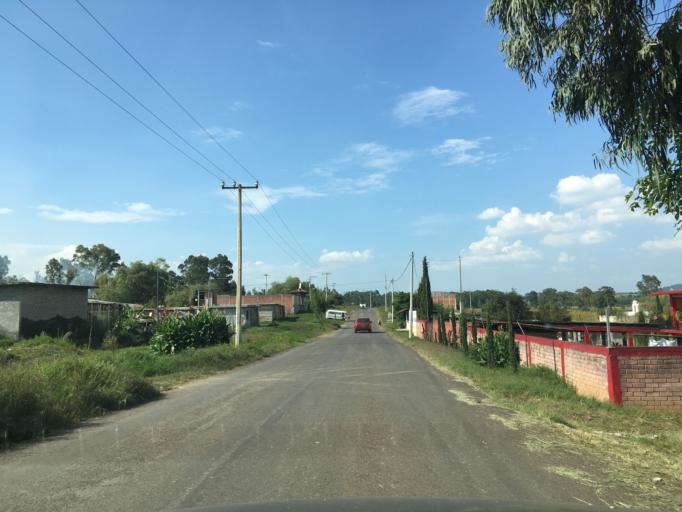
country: MX
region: Michoacan
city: Acuitzio del Canje
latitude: 19.5634
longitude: -101.2753
